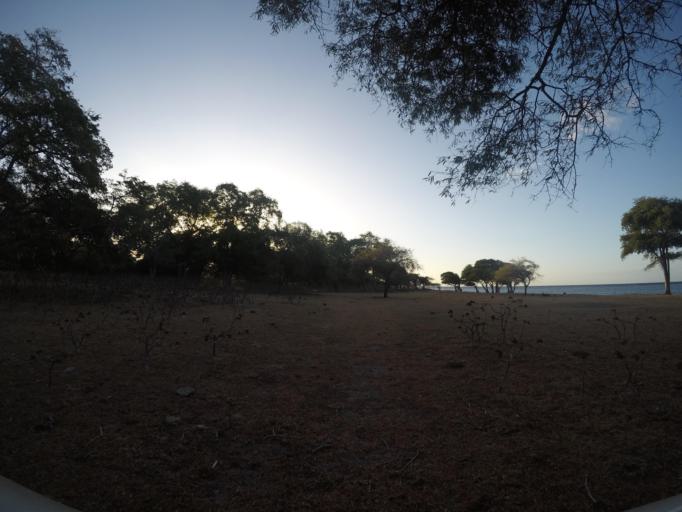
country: TL
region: Lautem
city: Lospalos
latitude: -8.3262
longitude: 127.0057
